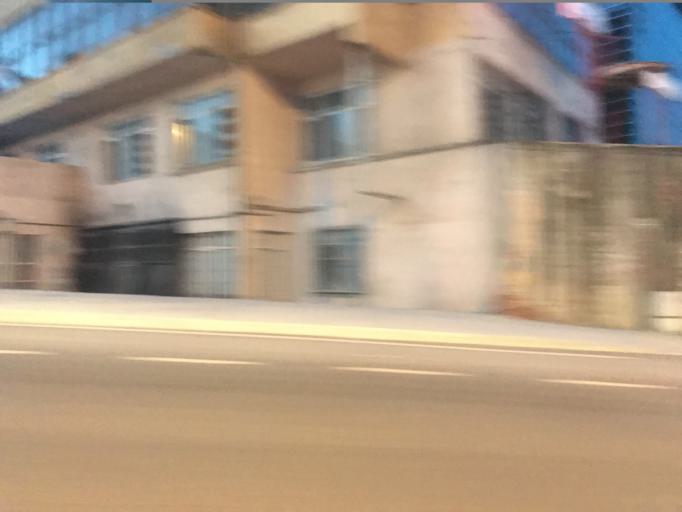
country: TR
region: Istanbul
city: Pendik
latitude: 40.9000
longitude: 29.2567
